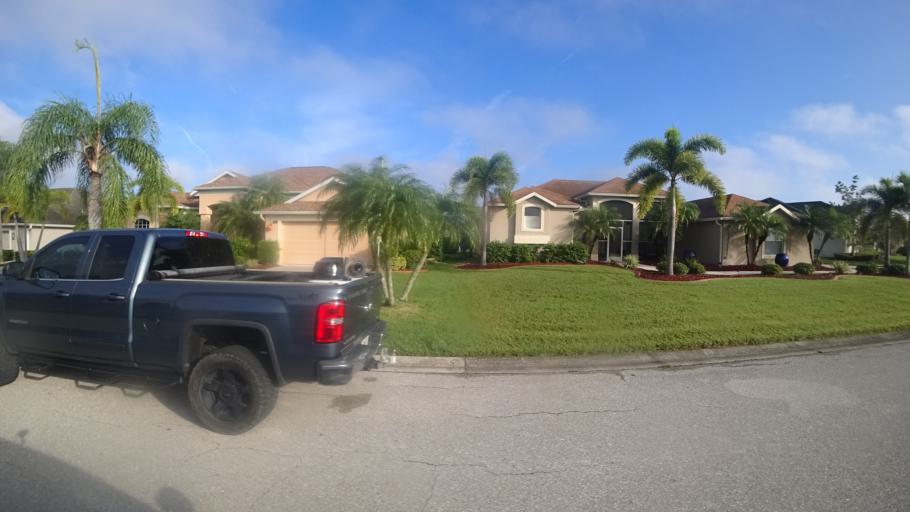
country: US
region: Florida
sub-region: Manatee County
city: Ellenton
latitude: 27.5391
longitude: -82.4762
